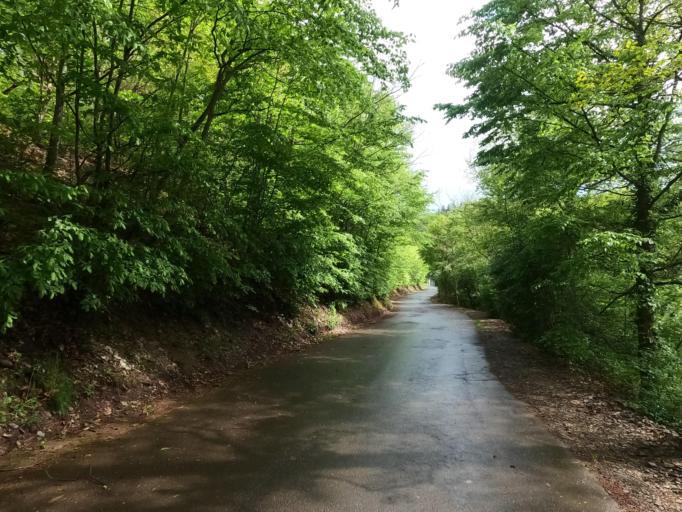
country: DE
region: Rheinland-Pfalz
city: Wierschem
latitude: 50.2089
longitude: 7.3367
